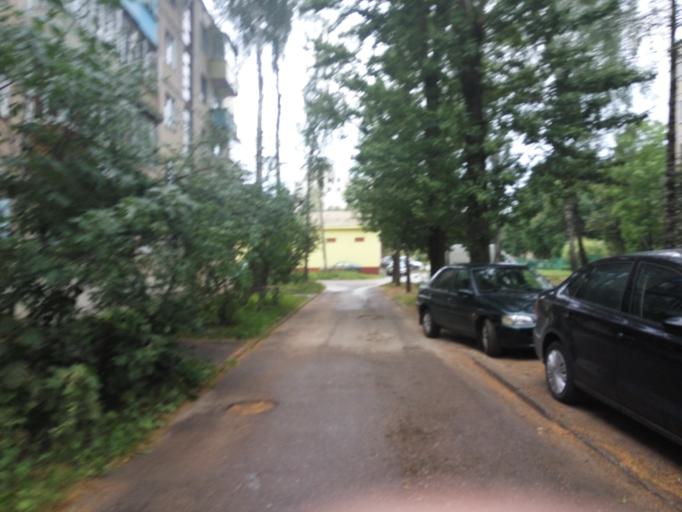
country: BY
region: Vitebsk
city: Vitebsk
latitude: 55.1978
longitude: 30.2476
